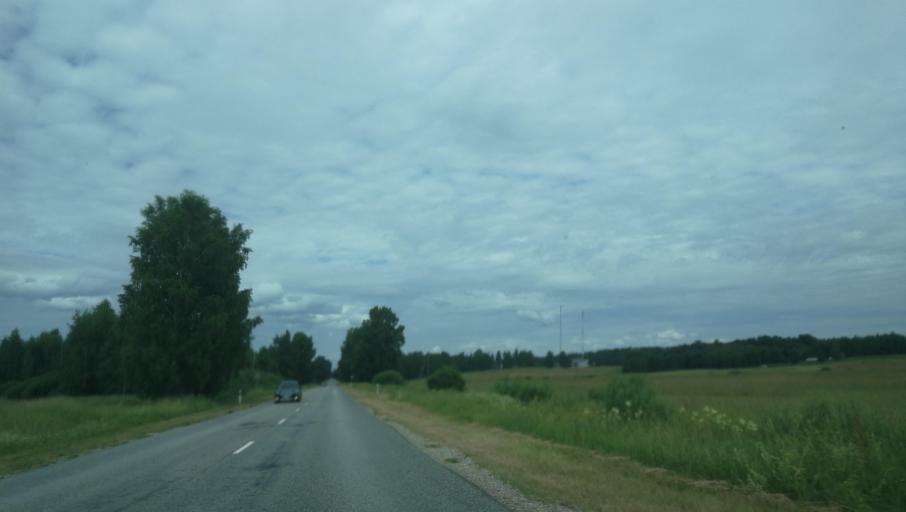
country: LV
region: Valmieras Rajons
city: Valmiera
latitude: 57.7091
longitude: 25.4257
